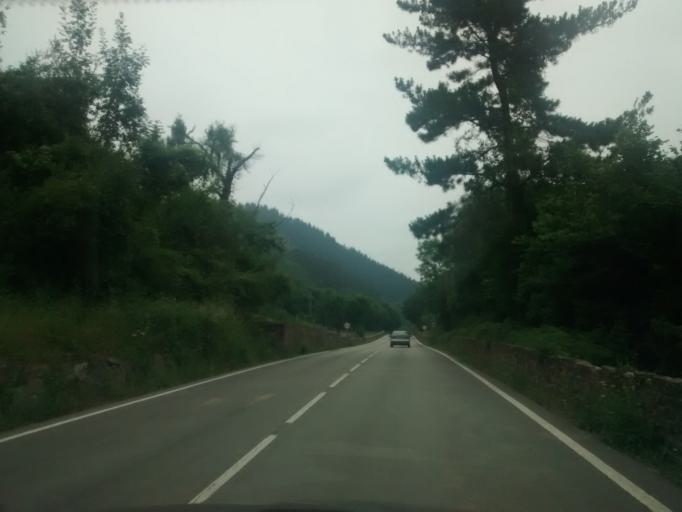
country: ES
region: Cantabria
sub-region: Provincia de Cantabria
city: Ruente
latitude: 43.1958
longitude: -4.3060
